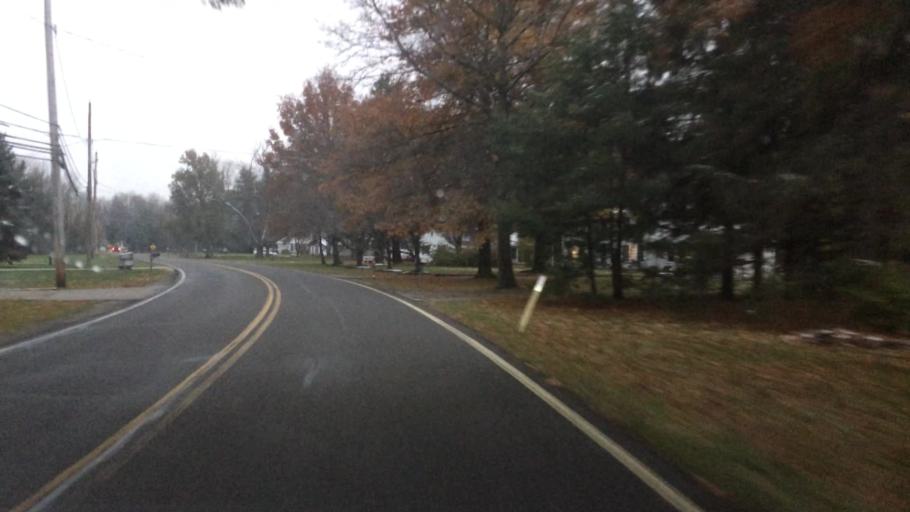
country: US
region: Ohio
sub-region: Cuyahoga County
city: Olmsted Falls
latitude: 41.3535
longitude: -81.9258
